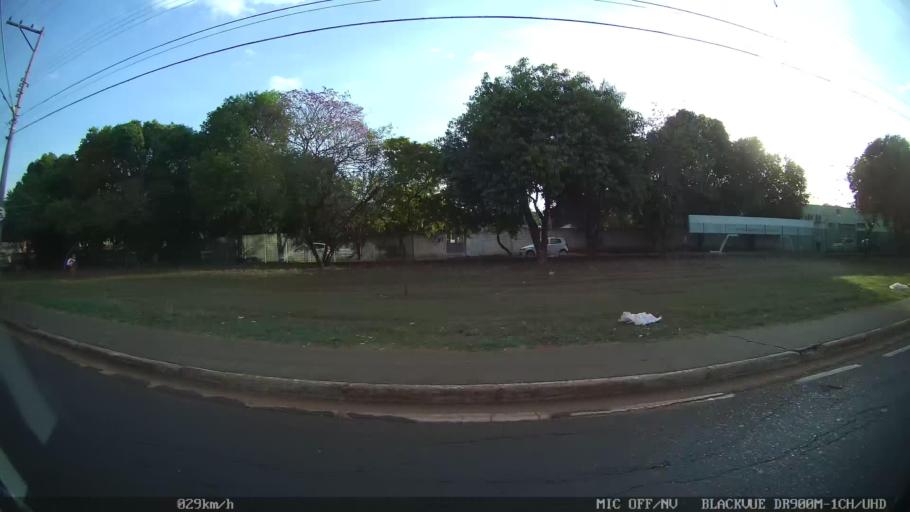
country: BR
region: Sao Paulo
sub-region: Ribeirao Preto
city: Ribeirao Preto
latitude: -21.1395
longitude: -47.8040
